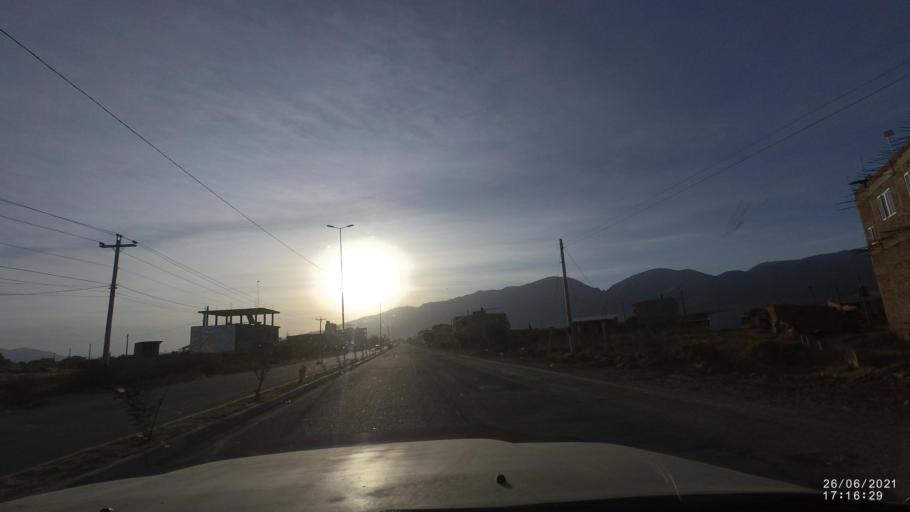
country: BO
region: Cochabamba
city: Cliza
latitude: -17.5587
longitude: -65.9384
